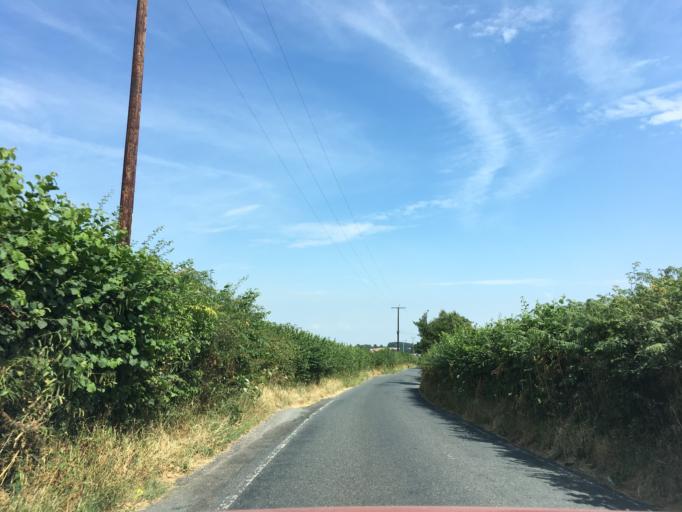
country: GB
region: Wales
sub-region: Newport
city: Langstone
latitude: 51.6130
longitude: -2.8968
